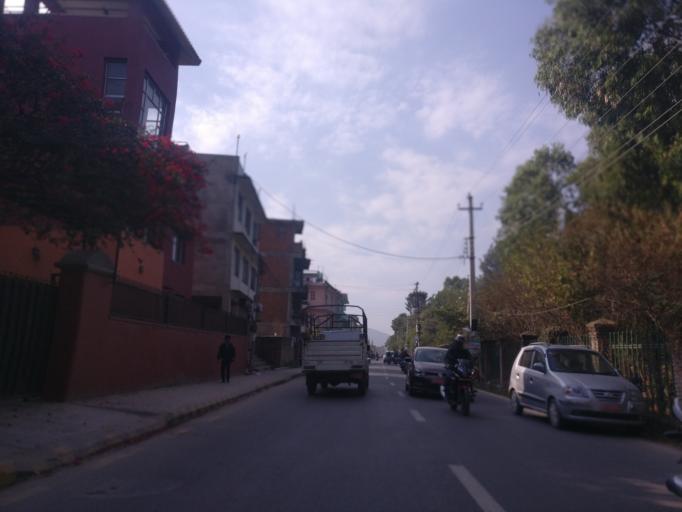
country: NP
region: Central Region
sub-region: Bagmati Zone
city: Patan
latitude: 27.6850
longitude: 85.3256
